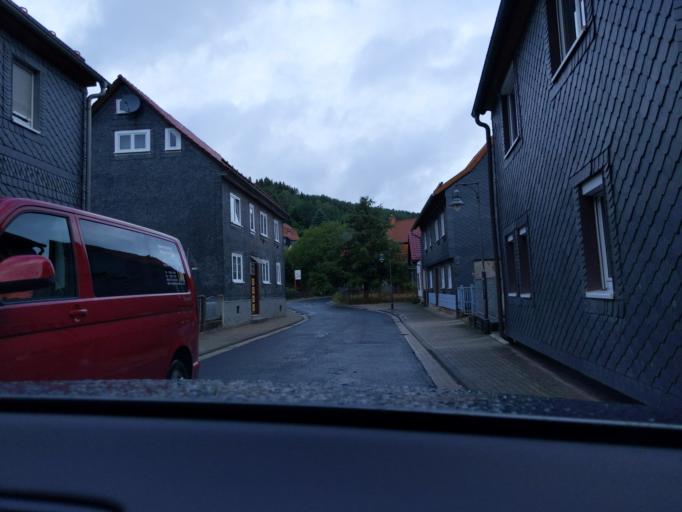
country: DE
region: Thuringia
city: Suhl
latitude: 50.6001
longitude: 10.6553
